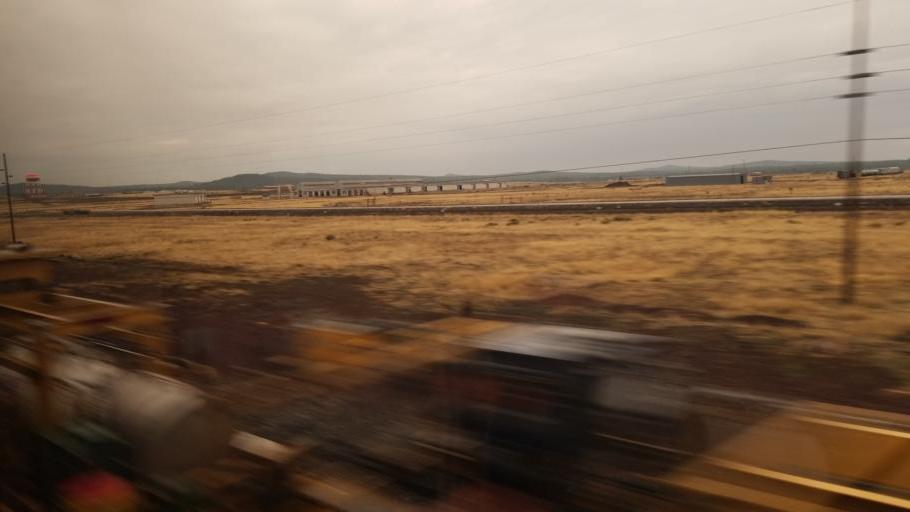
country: US
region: Arizona
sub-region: Coconino County
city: Parks
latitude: 35.2371
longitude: -111.8386
